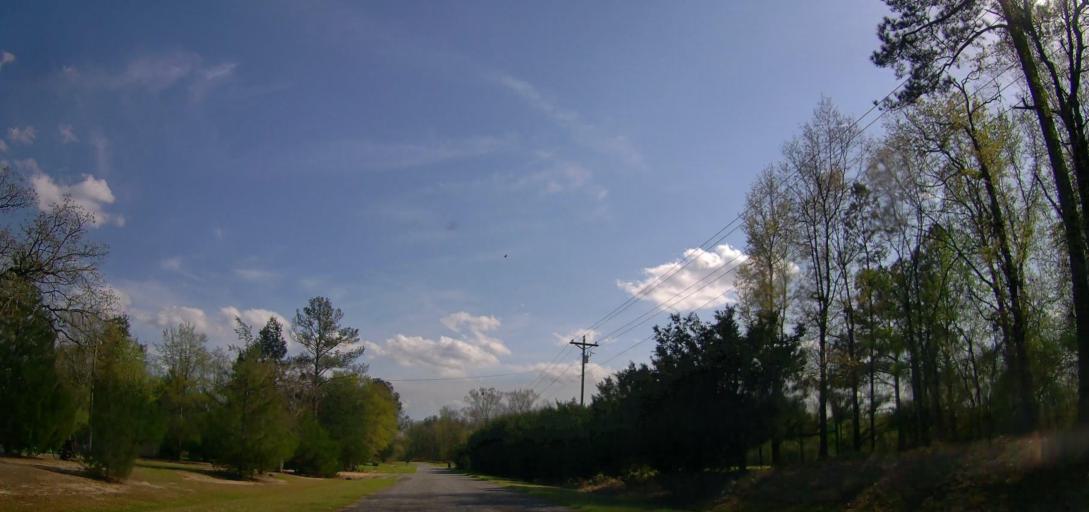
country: US
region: Georgia
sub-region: Baldwin County
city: Hardwick
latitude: 33.0310
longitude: -83.1191
